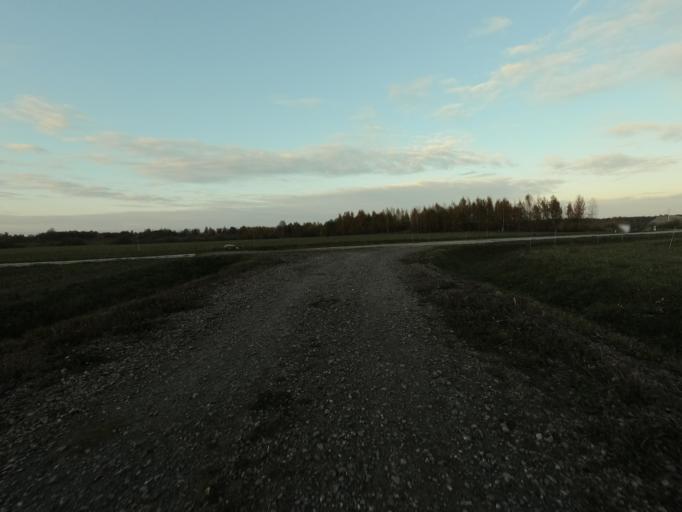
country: RU
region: Leningrad
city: Mga
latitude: 59.7893
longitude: 31.2004
